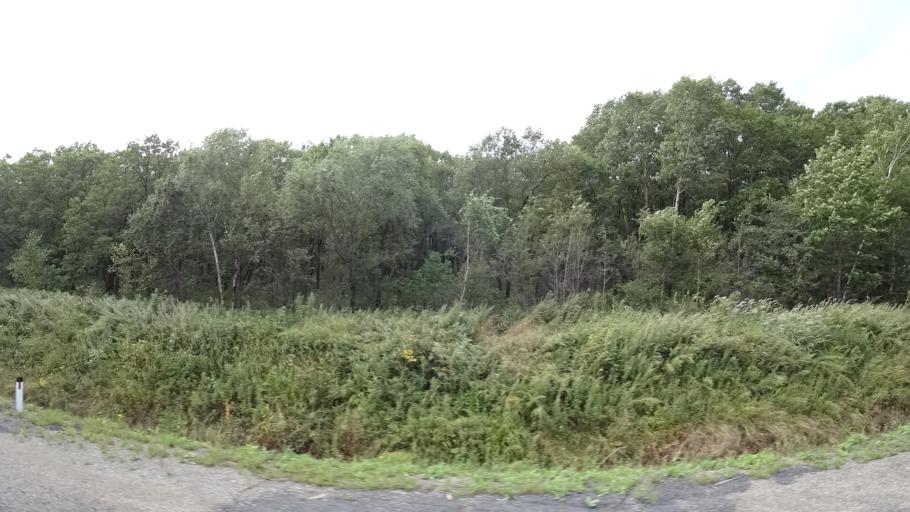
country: RU
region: Primorskiy
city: Lyalichi
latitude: 44.1035
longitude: 132.4236
